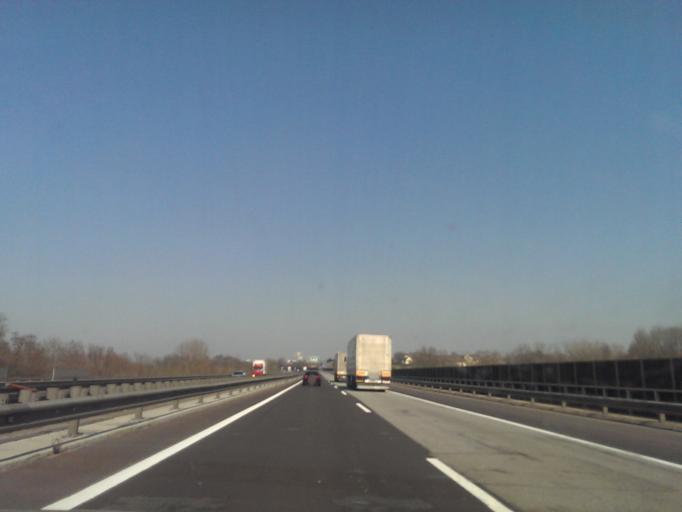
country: AT
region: Upper Austria
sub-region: Politischer Bezirk Scharding
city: Sankt Marienkirchen bei Schaerding
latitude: 48.3825
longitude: 13.4195
